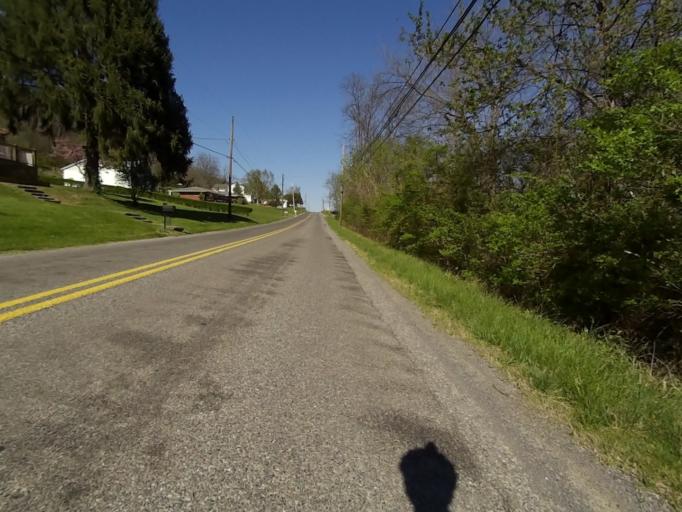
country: US
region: Pennsylvania
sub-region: Centre County
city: Bellefonte
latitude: 40.9042
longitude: -77.8198
